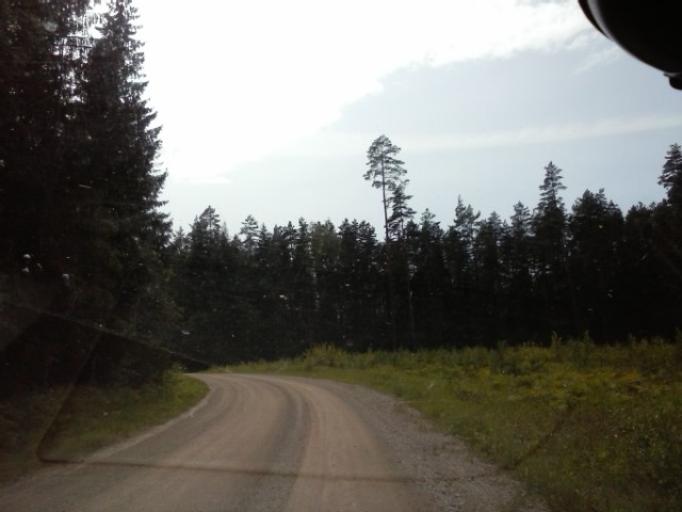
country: EE
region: Polvamaa
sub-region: Polva linn
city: Polva
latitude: 58.2492
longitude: 26.9649
